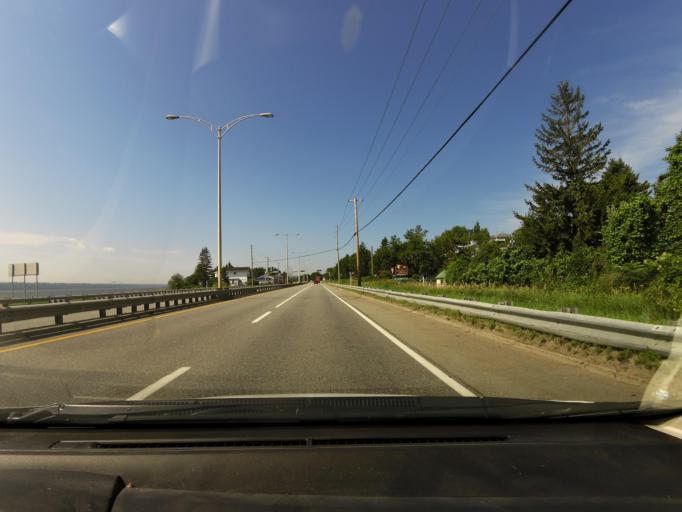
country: CA
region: Quebec
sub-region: Capitale-Nationale
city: Chateau-Richer
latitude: 46.9675
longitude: -71.0205
